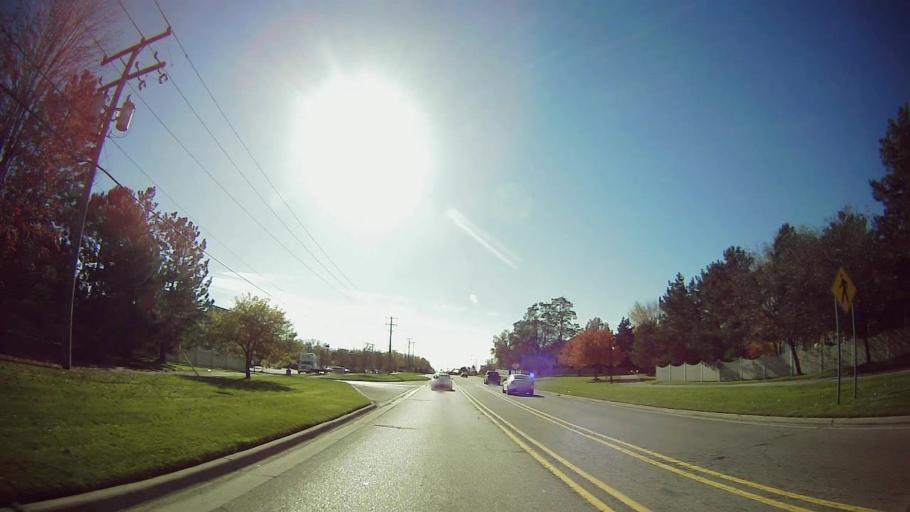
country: US
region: Michigan
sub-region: Oakland County
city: West Bloomfield Township
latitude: 42.5303
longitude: -83.3797
